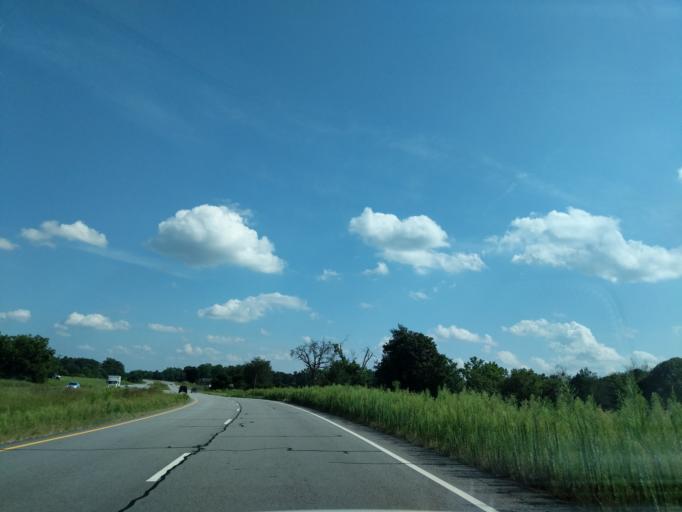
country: US
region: Georgia
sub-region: Banks County
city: Homer
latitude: 34.3843
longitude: -83.4850
